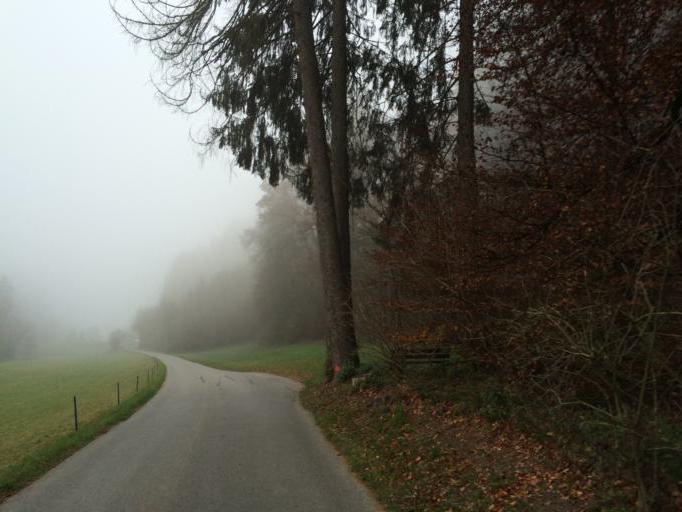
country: CH
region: Bern
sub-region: Bern-Mittelland District
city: Koniz
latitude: 46.9133
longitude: 7.4314
